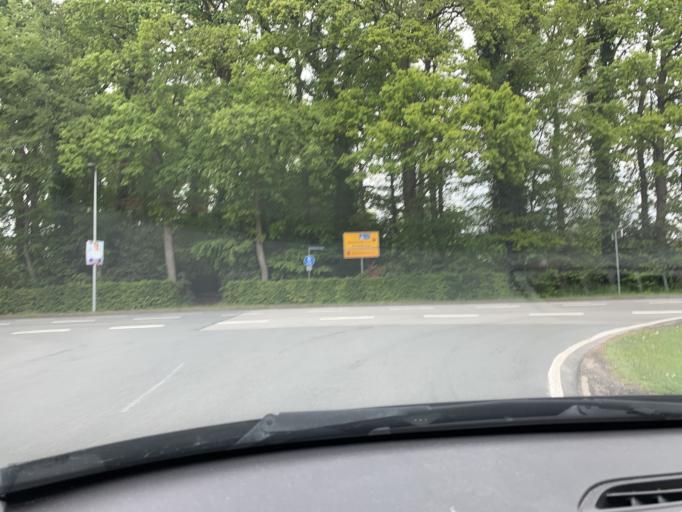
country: DE
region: Lower Saxony
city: Bad Zwischenahn
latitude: 53.1954
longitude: 8.0452
